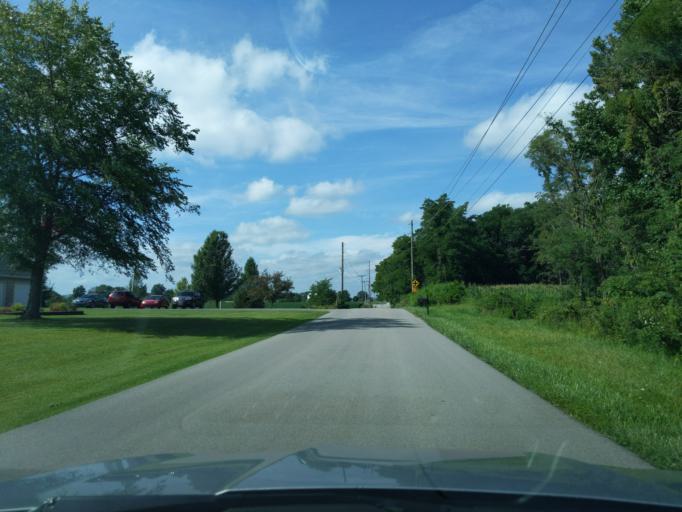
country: US
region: Indiana
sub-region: Ripley County
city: Osgood
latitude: 39.2484
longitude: -85.3474
